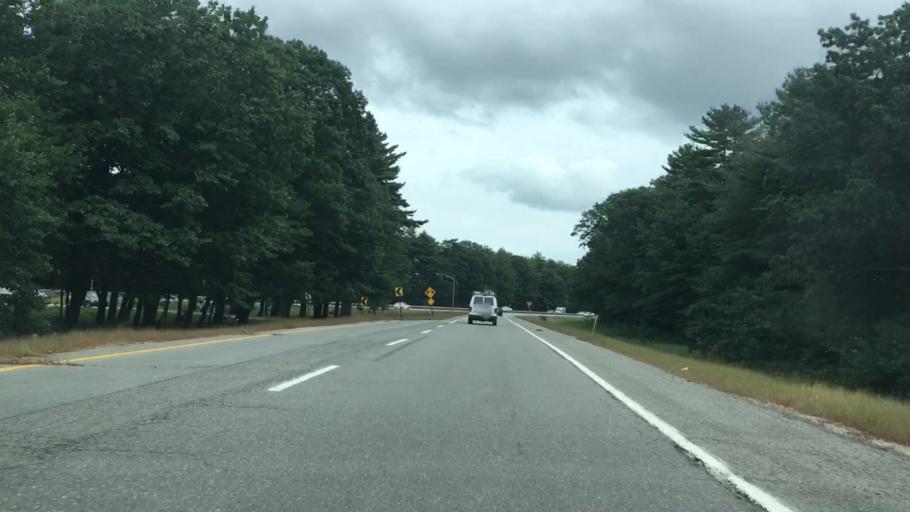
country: US
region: Maine
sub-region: Cumberland County
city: South Portland Gardens
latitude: 43.6283
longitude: -70.3365
